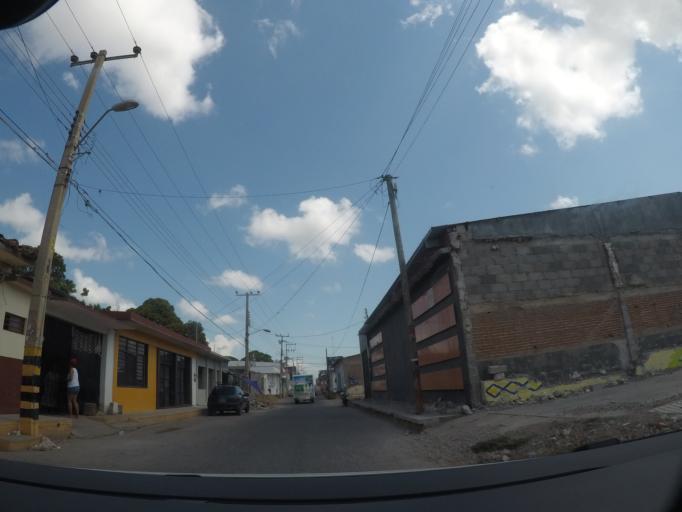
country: MX
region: Oaxaca
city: Juchitan de Zaragoza
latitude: 16.4376
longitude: -95.0210
